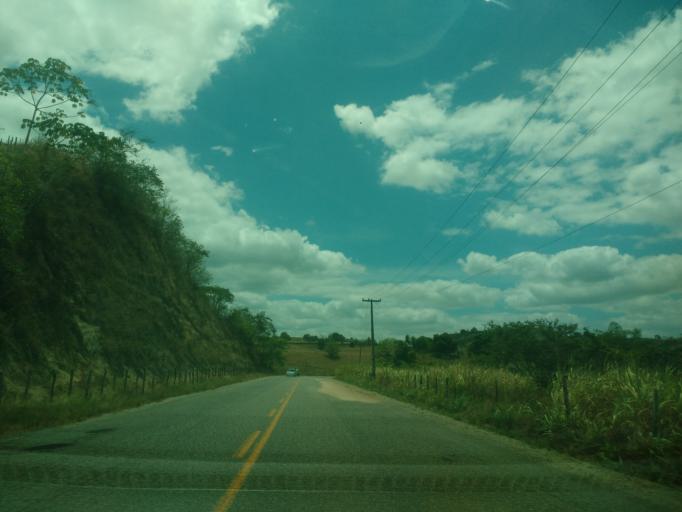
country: BR
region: Alagoas
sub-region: Santana Do Mundau
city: Santana do Mundau
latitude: -9.1452
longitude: -36.1647
